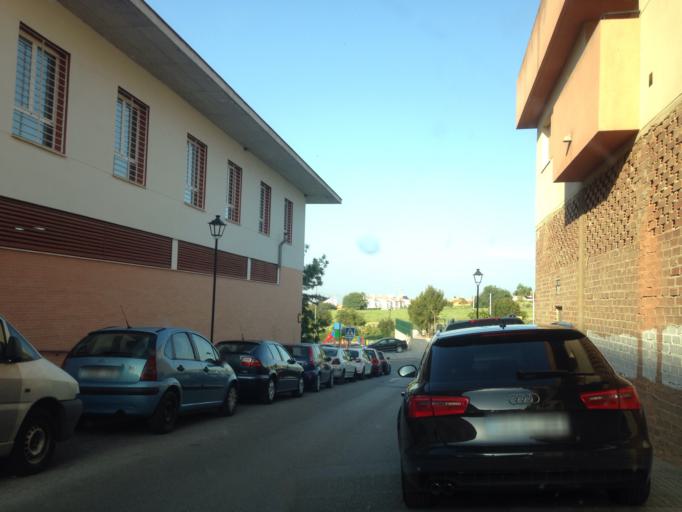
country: ES
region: Andalusia
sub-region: Provincia de Malaga
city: Alhaurin de la Torre
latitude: 36.6617
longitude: -4.5589
